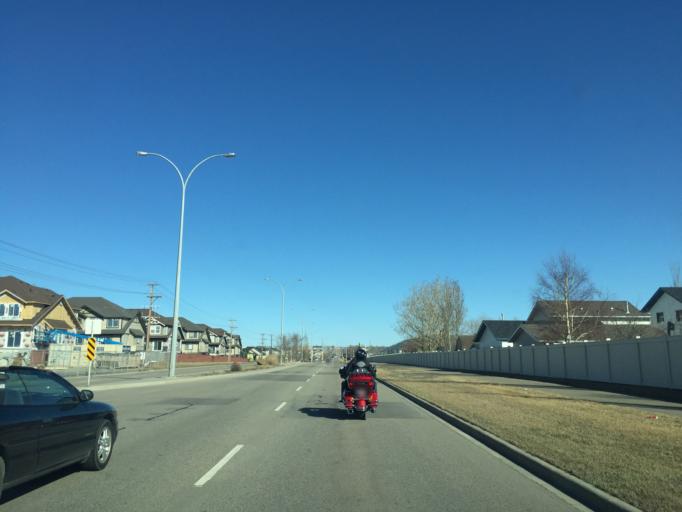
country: CA
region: Alberta
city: Airdrie
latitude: 51.3000
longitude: -114.0373
